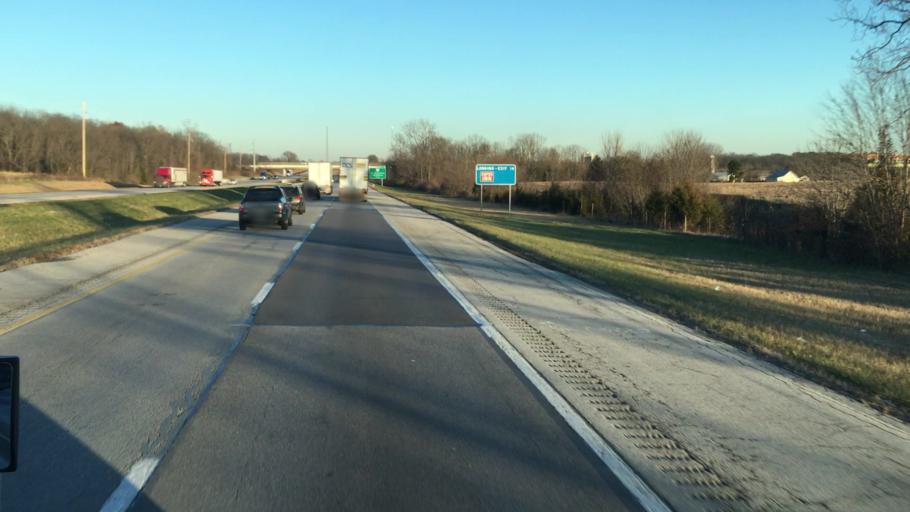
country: US
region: Ohio
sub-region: Preble County
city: Lewisburg
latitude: 39.8363
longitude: -84.5662
